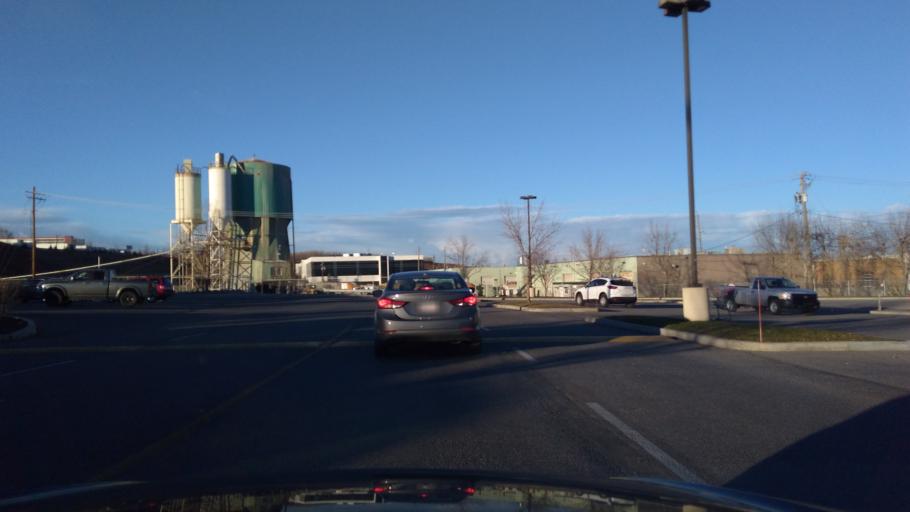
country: CA
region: Alberta
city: Calgary
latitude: 50.9895
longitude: -114.0439
